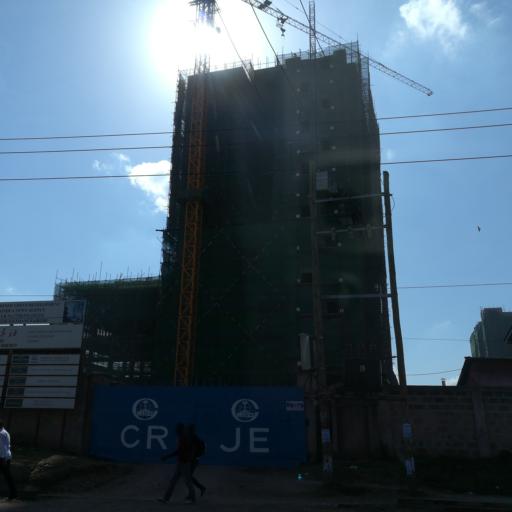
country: KE
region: Nairobi Area
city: Nairobi
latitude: -1.2971
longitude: 36.7880
